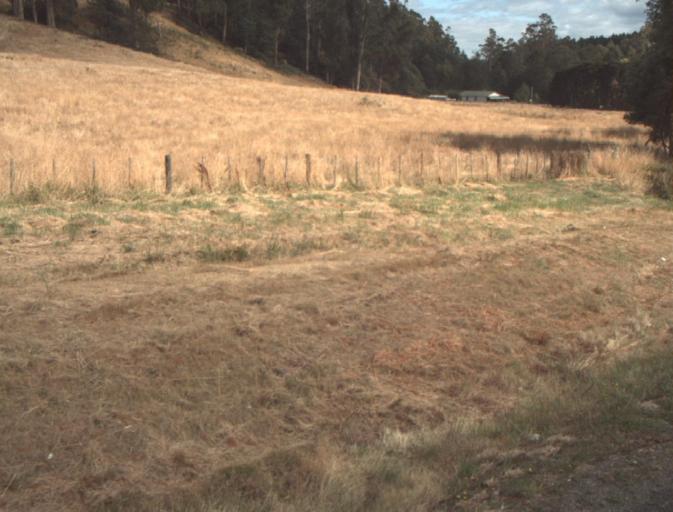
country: AU
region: Tasmania
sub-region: Launceston
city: Mayfield
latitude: -41.2795
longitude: 147.2202
